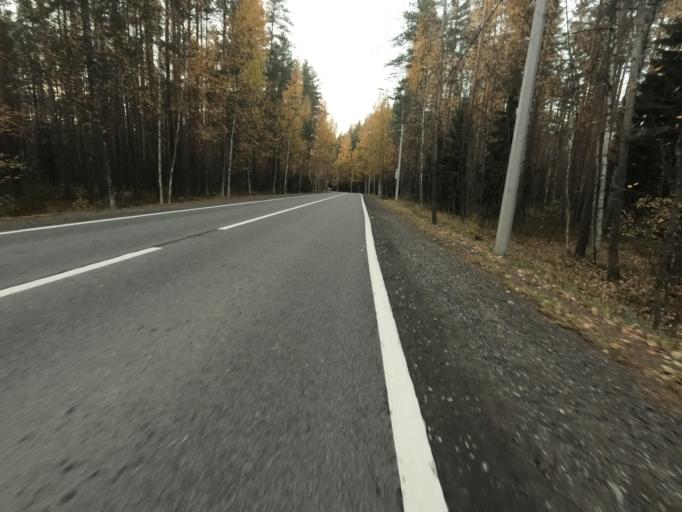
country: RU
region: St.-Petersburg
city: Repino
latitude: 60.1885
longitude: 29.8640
